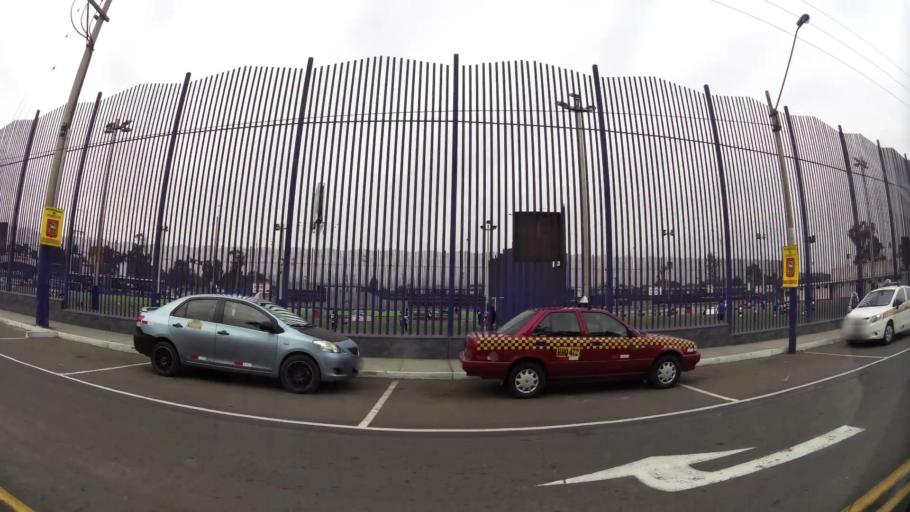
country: PE
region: Lima
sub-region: Lima
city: Surco
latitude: -12.1686
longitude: -77.0193
